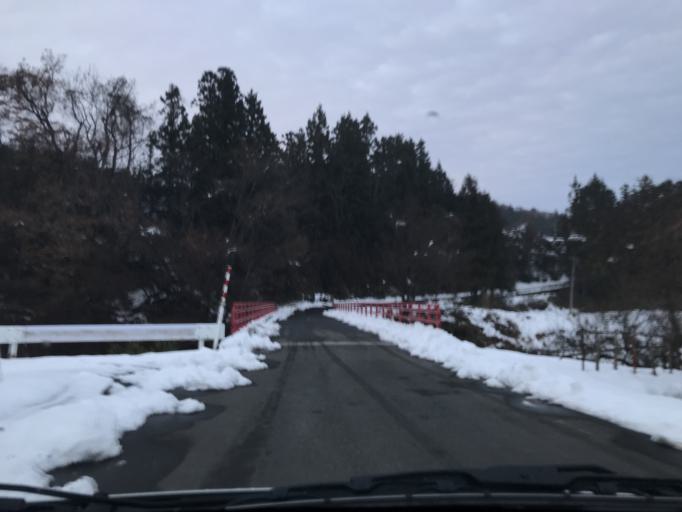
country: JP
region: Iwate
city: Mizusawa
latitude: 39.0586
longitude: 141.0342
